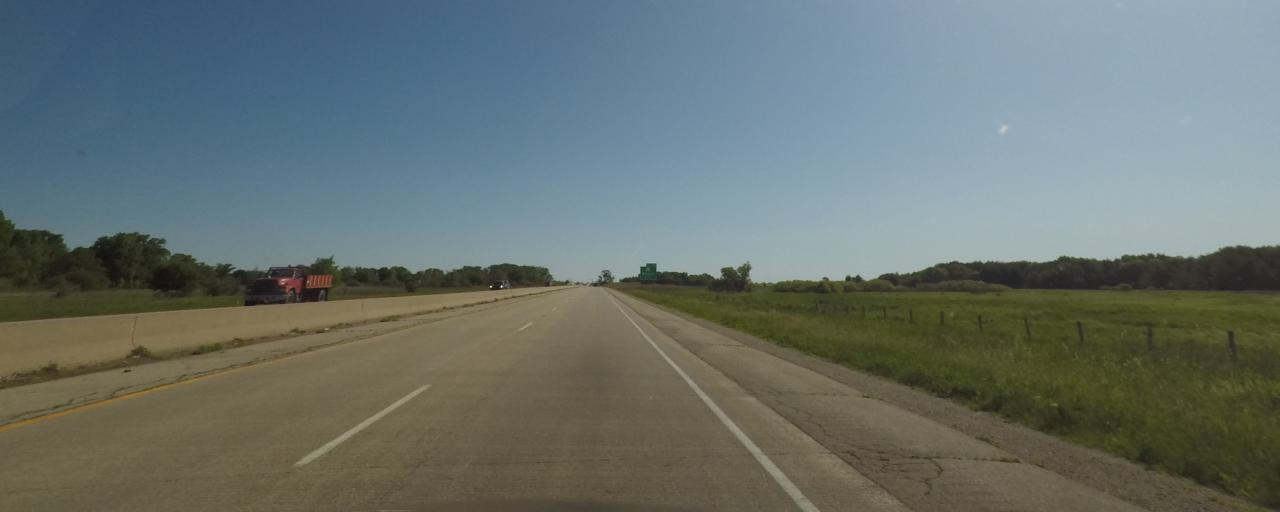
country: US
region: Wisconsin
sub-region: Fond du Lac County
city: Waupun
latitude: 43.5877
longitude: -88.7448
